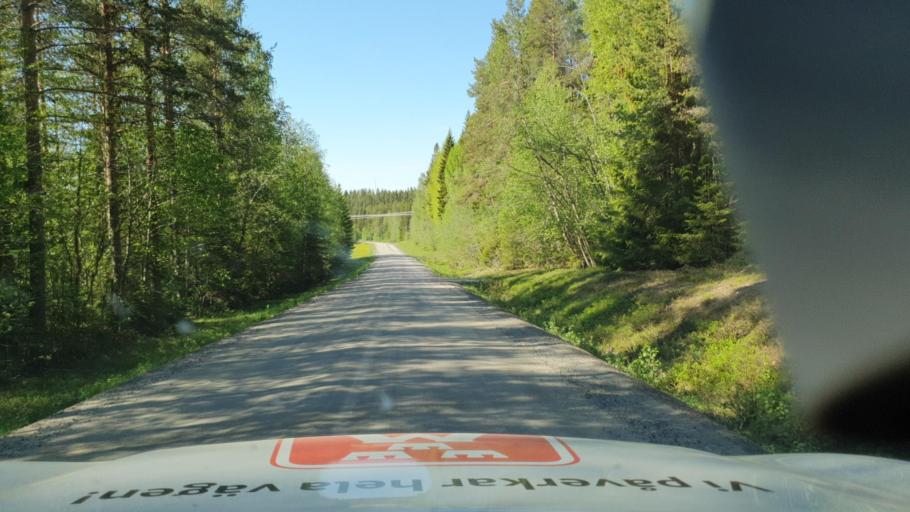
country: SE
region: Vaesterbotten
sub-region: Vannas Kommun
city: Vaennaes
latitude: 64.0077
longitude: 19.7312
